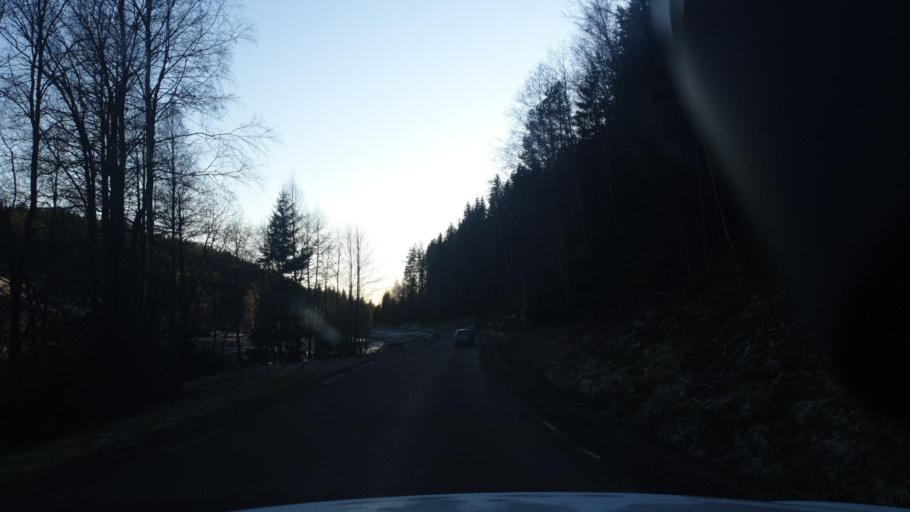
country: SE
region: Vaermland
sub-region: Arvika Kommun
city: Arvika
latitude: 59.7015
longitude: 12.7913
